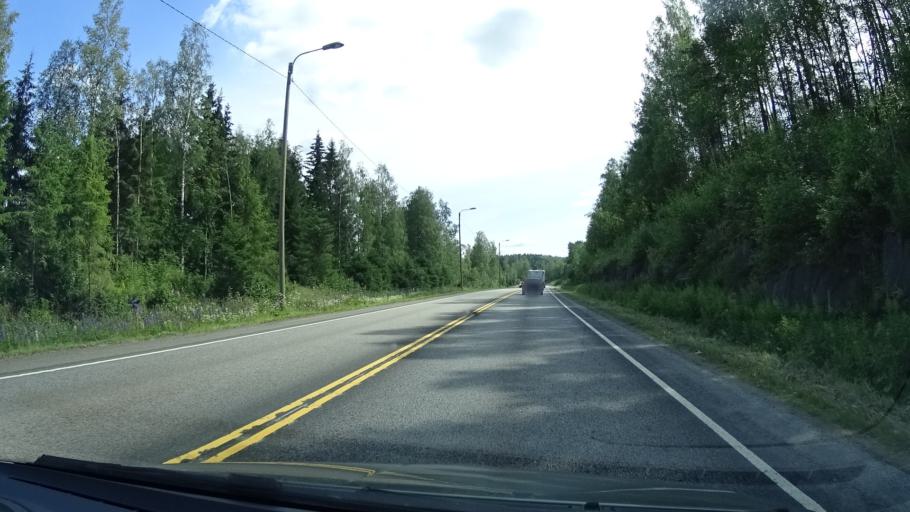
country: FI
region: Central Finland
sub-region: Jyvaeskylae
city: Jyvaeskylae
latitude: 62.2682
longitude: 25.5527
